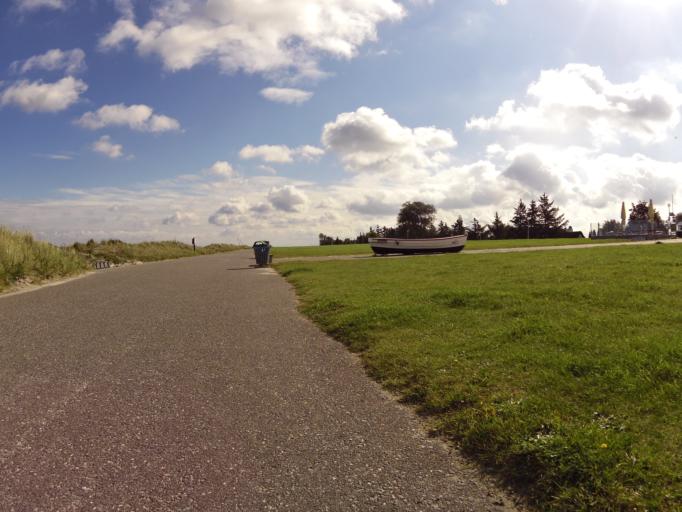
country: DE
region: Schleswig-Holstein
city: Wisch
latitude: 54.4274
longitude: 10.3778
